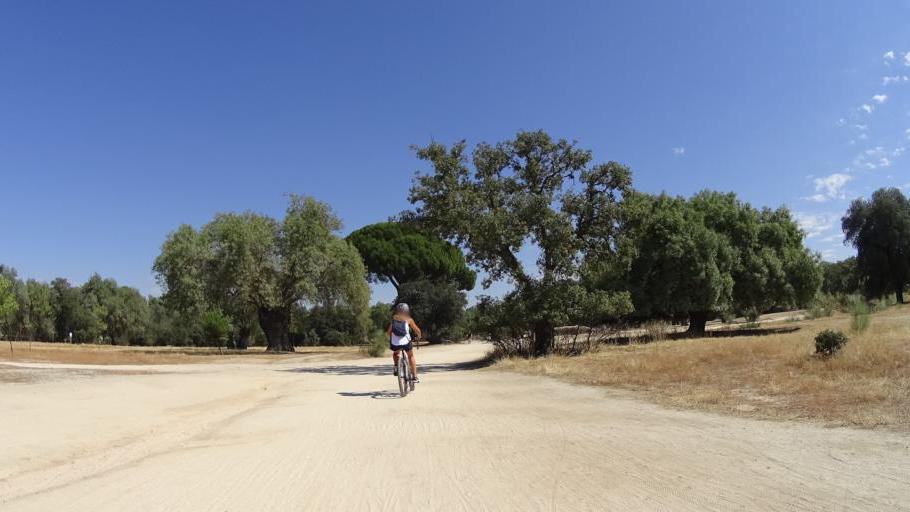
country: ES
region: Madrid
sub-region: Provincia de Madrid
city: Boadilla del Monte
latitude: 40.4129
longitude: -3.8645
